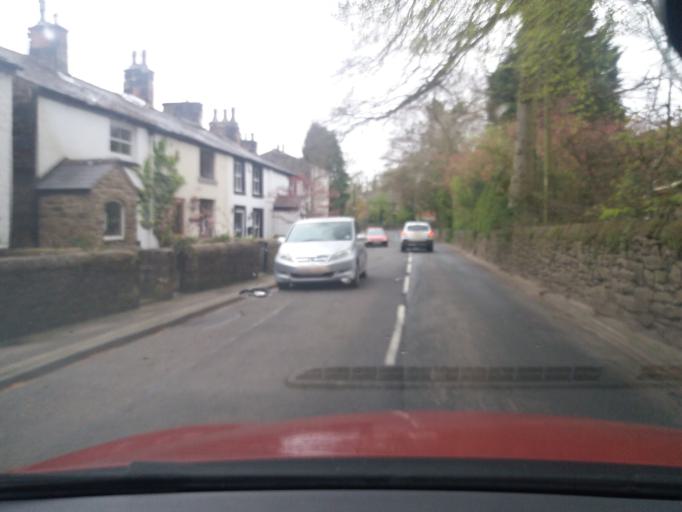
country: GB
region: England
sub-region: Lancashire
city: Clayton-le-Woods
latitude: 53.6853
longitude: -2.6366
